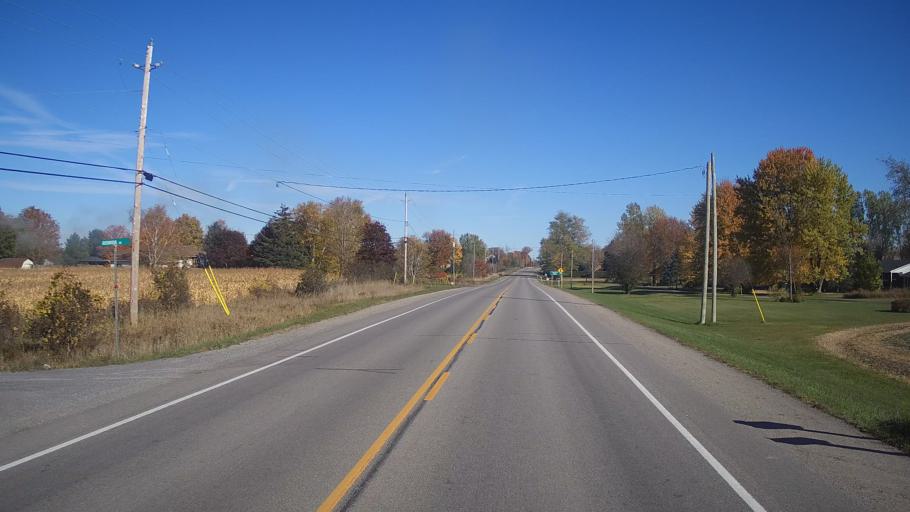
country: CA
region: Ontario
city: Kingston
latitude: 44.4073
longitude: -76.5628
